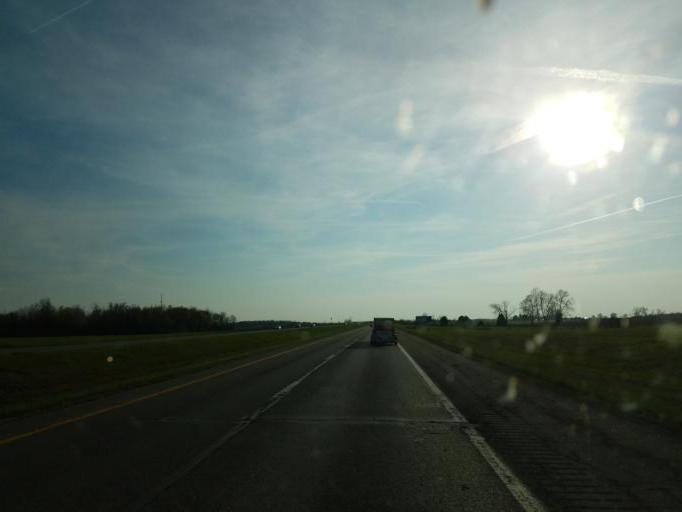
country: US
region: Ohio
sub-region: Clinton County
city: Wilmington
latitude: 39.4923
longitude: -83.9233
